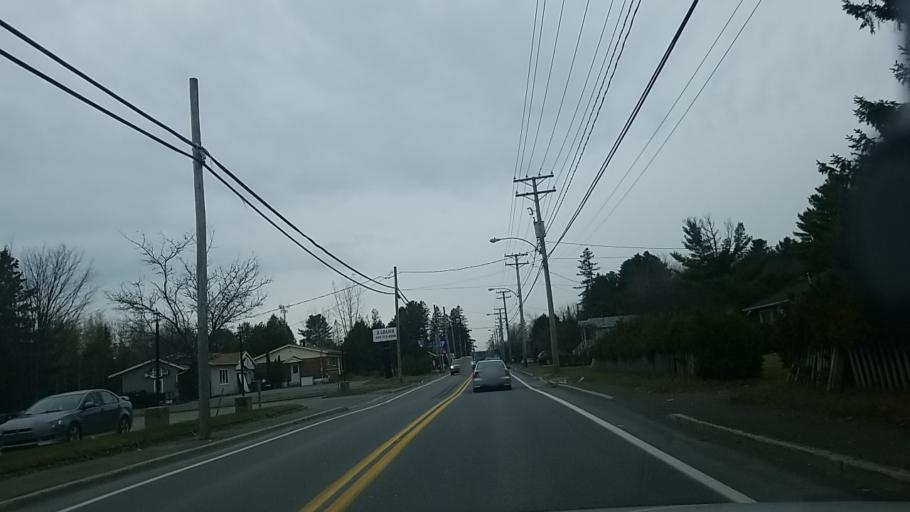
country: CA
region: Quebec
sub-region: Laurentides
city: Saint-Jerome
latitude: 45.7866
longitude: -74.0713
